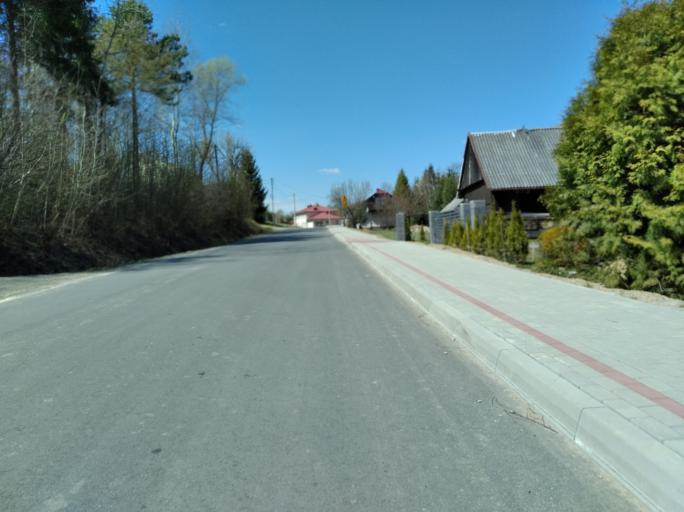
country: PL
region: Subcarpathian Voivodeship
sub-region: Powiat brzozowski
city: Jablonka
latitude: 49.7157
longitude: 22.1334
